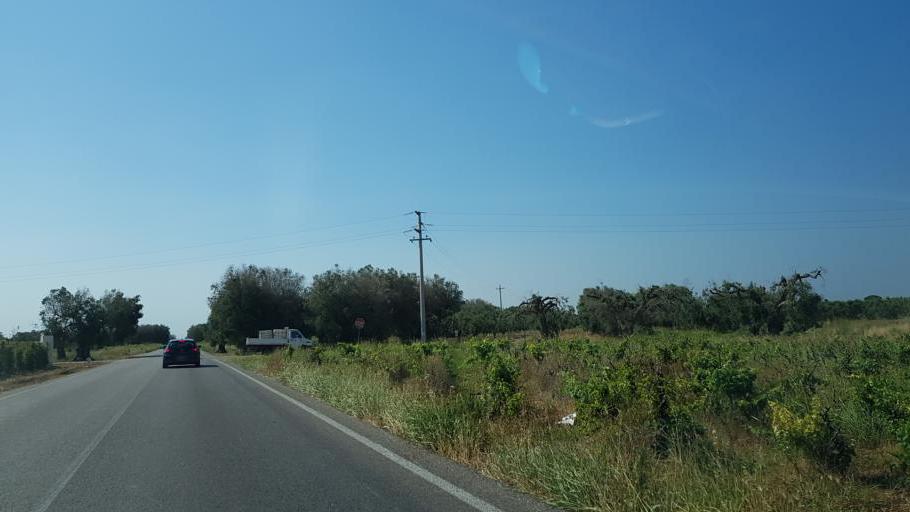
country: IT
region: Apulia
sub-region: Provincia di Lecce
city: Guagnano
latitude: 40.4062
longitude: 17.9657
